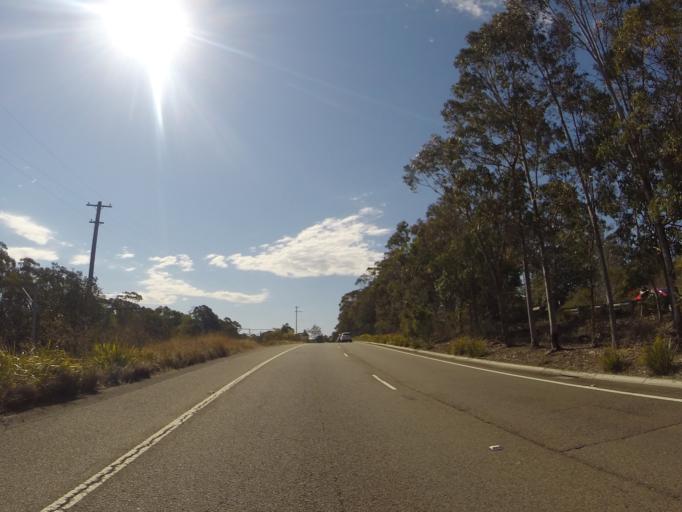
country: AU
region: New South Wales
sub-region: Blue Mountains Municipality
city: Blaxland
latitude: -33.7173
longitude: 150.5931
